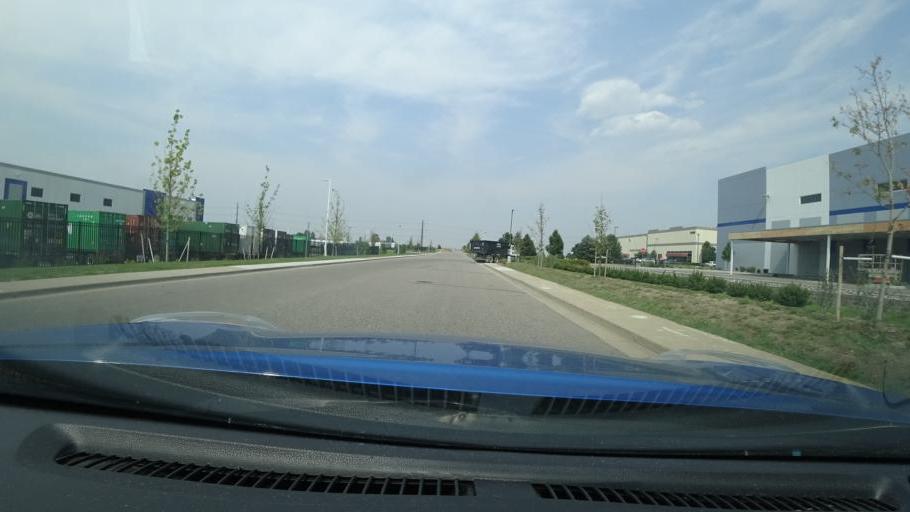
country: US
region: Colorado
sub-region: Adams County
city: Aurora
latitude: 39.7667
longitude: -104.7414
